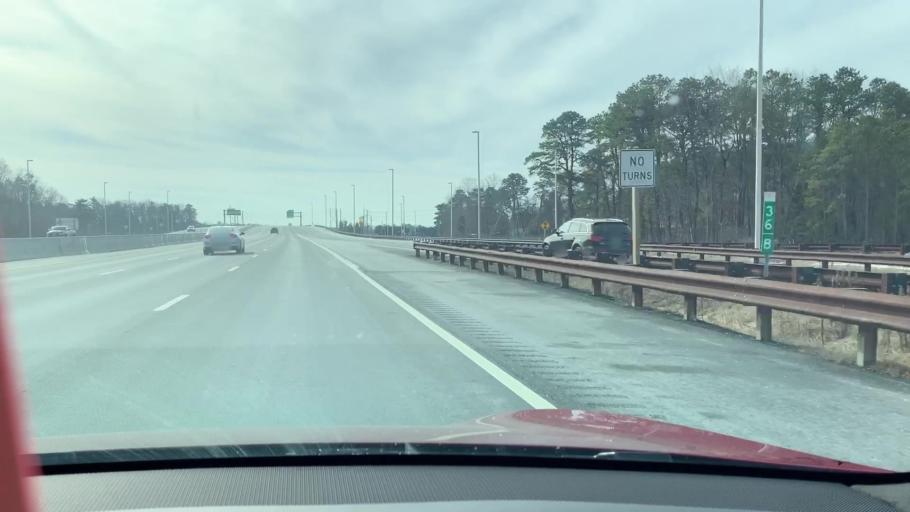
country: US
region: New Jersey
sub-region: Atlantic County
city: Pleasantville
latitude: 39.4082
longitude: -74.5562
